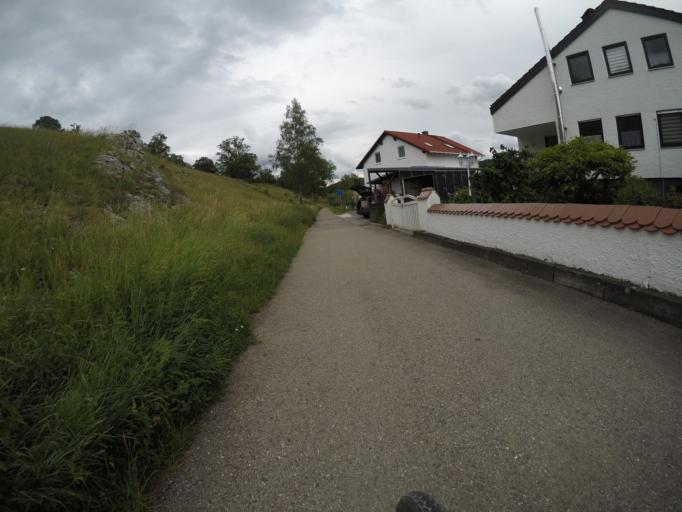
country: DE
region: Baden-Wuerttemberg
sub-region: Tuebingen Region
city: Westerstetten
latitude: 48.5194
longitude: 9.9595
